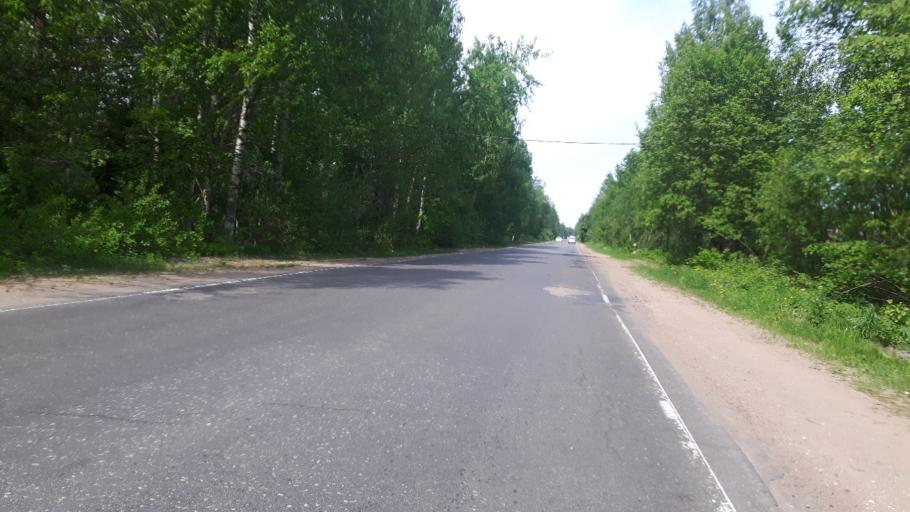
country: RU
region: Leningrad
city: Ust'-Luga
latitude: 59.6413
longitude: 28.2761
